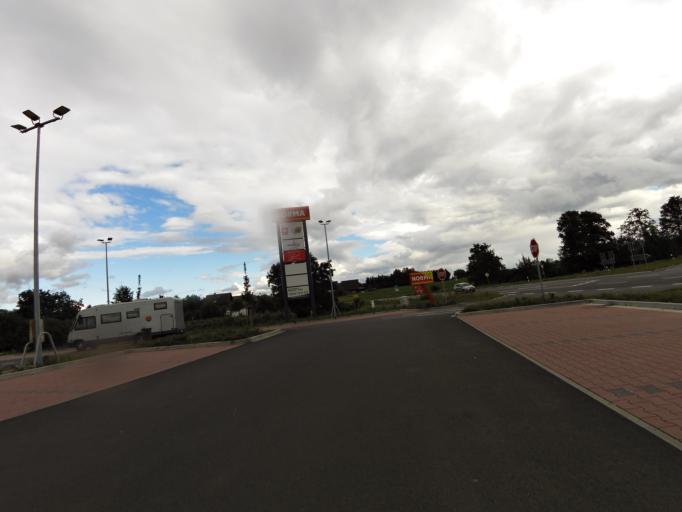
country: DE
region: North Rhine-Westphalia
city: Meckenheim
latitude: 50.5846
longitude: 7.0282
